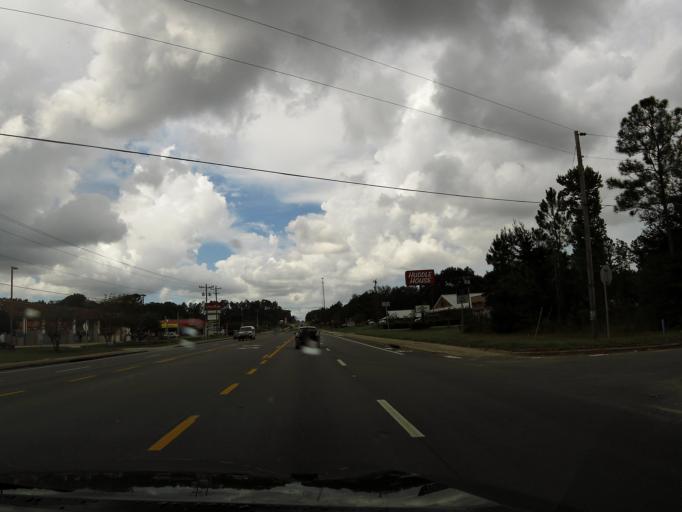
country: US
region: Florida
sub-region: Clay County
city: Middleburg
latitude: 30.0630
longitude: -81.8765
